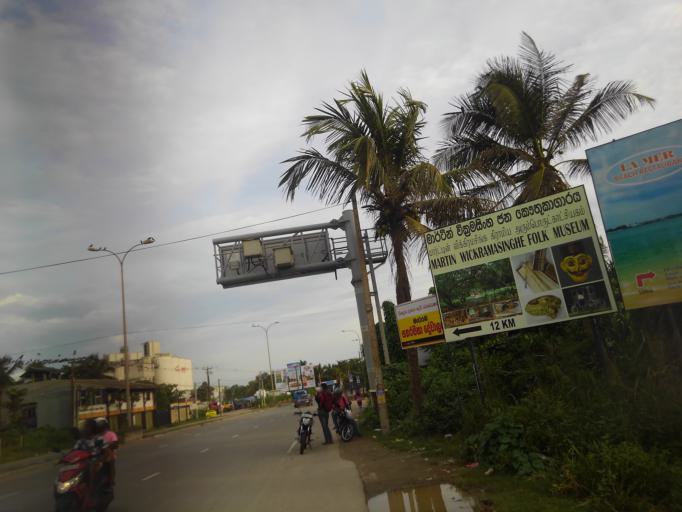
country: LK
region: Southern
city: Unawatuna
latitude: 6.0291
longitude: 80.2423
